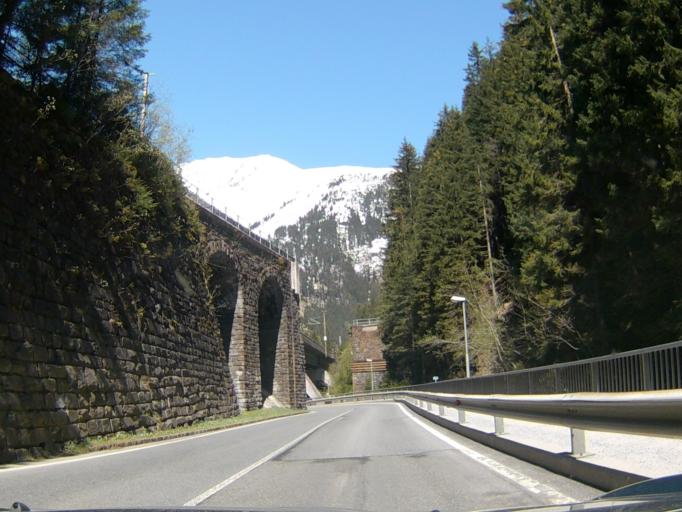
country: AT
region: Salzburg
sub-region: Politischer Bezirk Sankt Johann im Pongau
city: Bad Gastein
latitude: 47.0835
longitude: 13.1264
